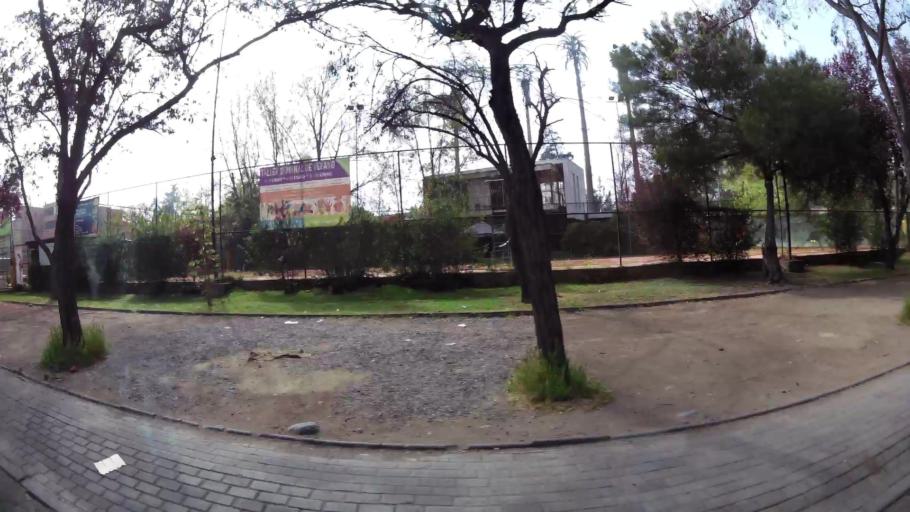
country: CL
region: Santiago Metropolitan
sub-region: Provincia de Santiago
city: Villa Presidente Frei, Nunoa, Santiago, Chile
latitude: -33.3808
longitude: -70.5688
